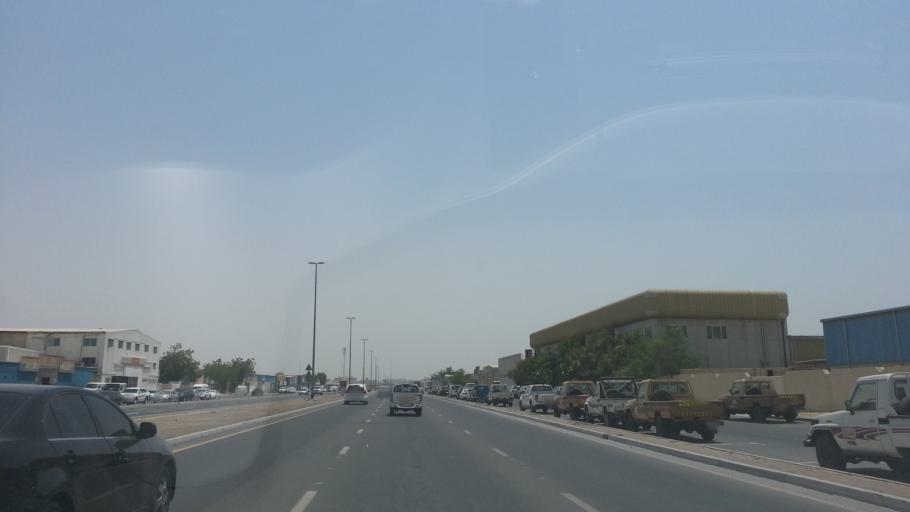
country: AE
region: Dubai
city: Dubai
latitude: 25.1187
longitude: 55.2234
